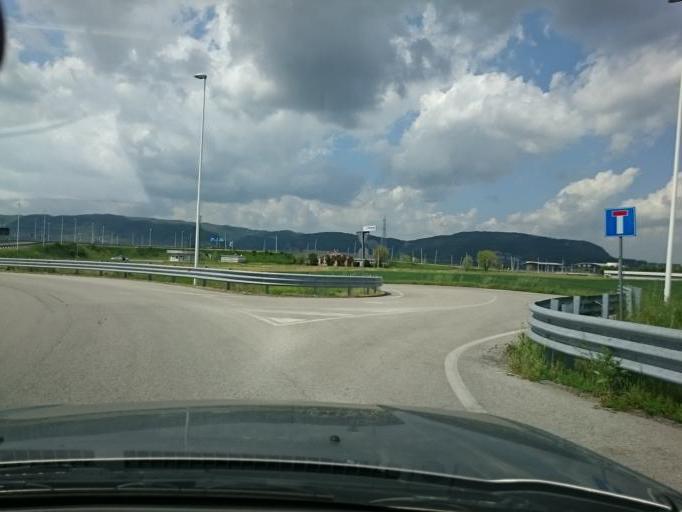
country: IT
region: Veneto
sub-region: Provincia di Vicenza
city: Villaganzerla
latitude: 45.4535
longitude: 11.6334
